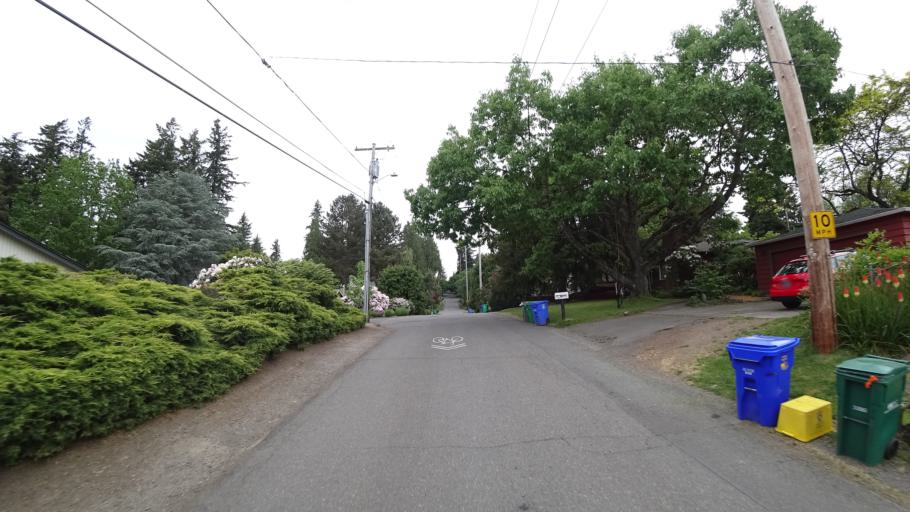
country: US
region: Oregon
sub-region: Washington County
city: Garden Home-Whitford
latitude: 45.4707
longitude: -122.7384
